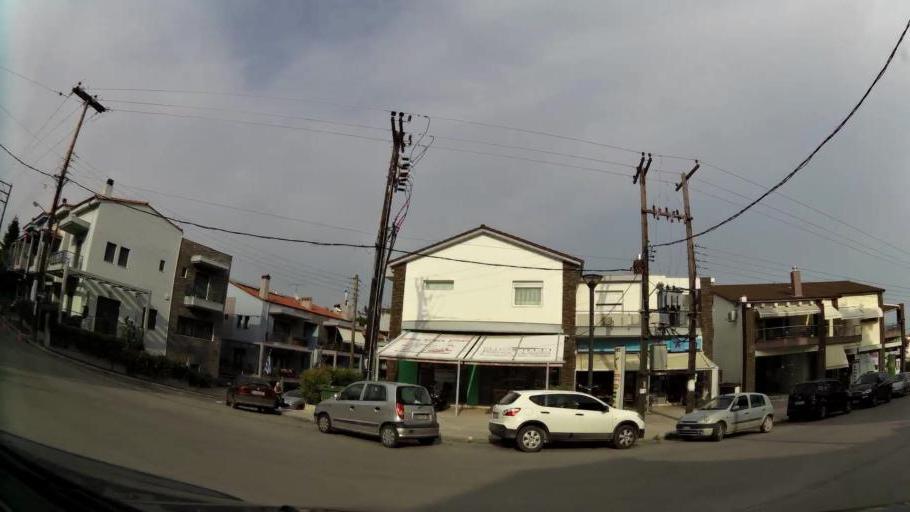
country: GR
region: Central Macedonia
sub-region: Nomos Thessalonikis
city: Oraiokastro
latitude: 40.7250
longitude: 22.9134
